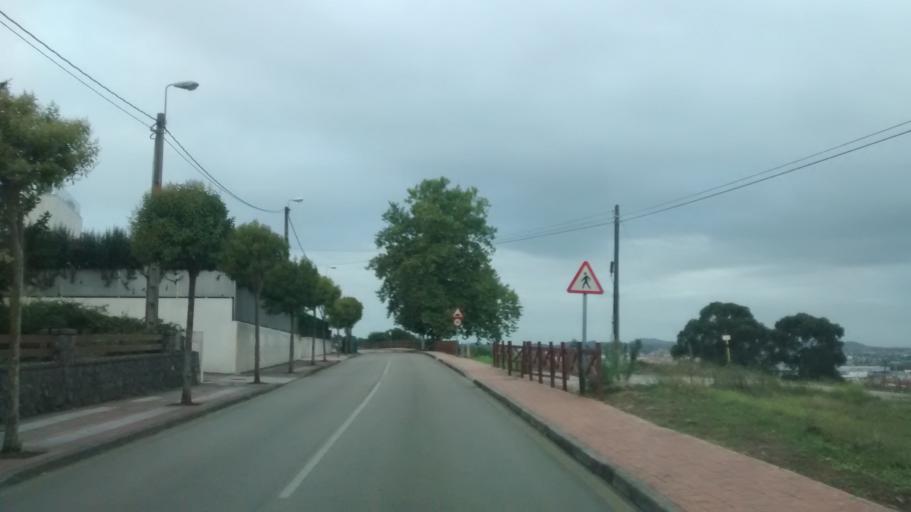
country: ES
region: Cantabria
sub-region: Provincia de Cantabria
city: El Astillero
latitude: 43.4199
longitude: -3.8225
